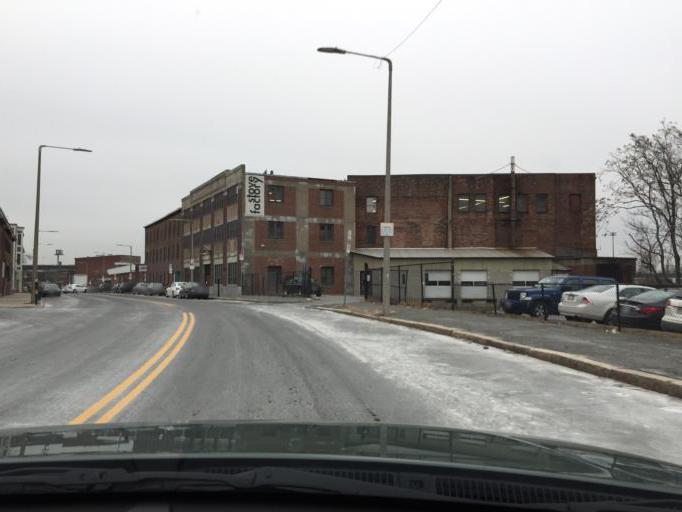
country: US
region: Massachusetts
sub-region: Suffolk County
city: Boston
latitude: 42.3837
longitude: -71.0685
